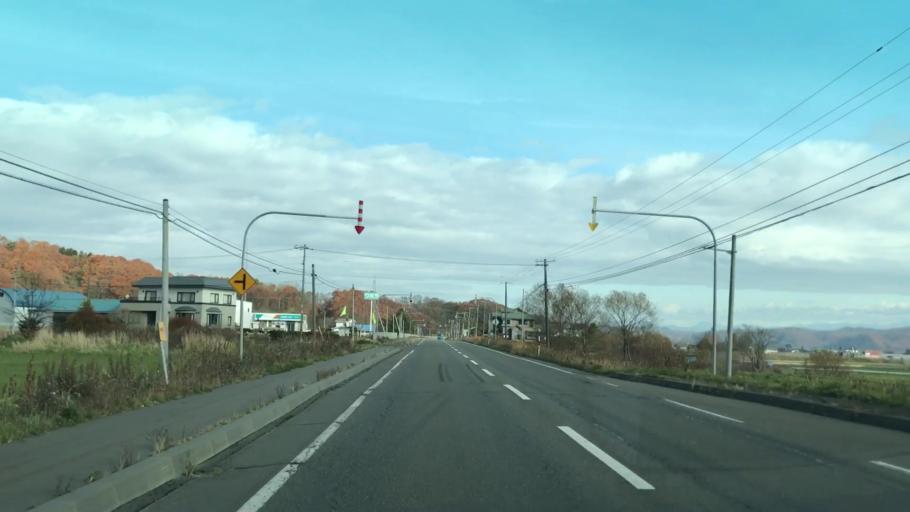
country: JP
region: Hokkaido
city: Shizunai-furukawacho
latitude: 42.5561
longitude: 142.0777
